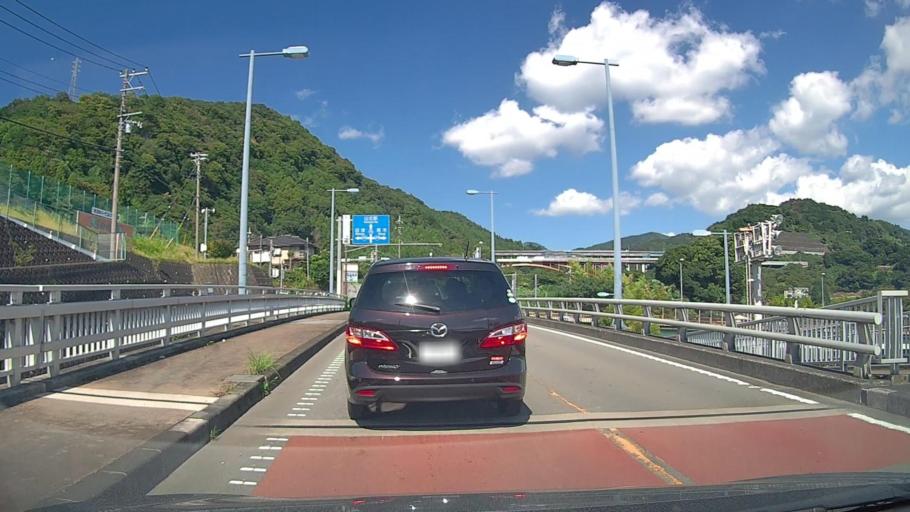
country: JP
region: Kanagawa
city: Odawara
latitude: 35.3570
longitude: 139.0686
